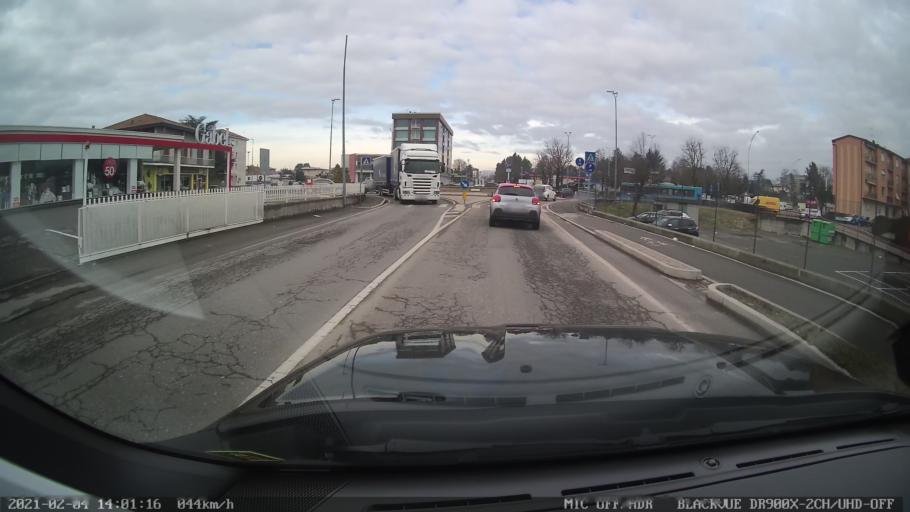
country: IT
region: Lombardy
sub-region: Provincia di Varese
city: Tradate
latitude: 45.7085
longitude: 8.9019
